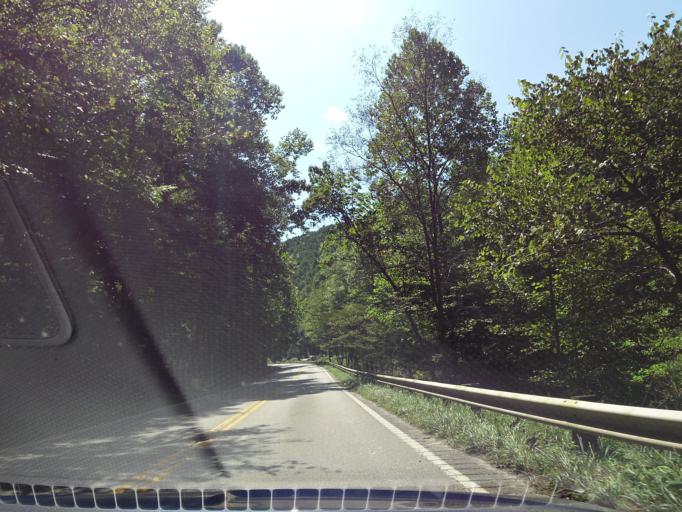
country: US
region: Kentucky
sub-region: Harlan County
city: Loyall
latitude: 36.9176
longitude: -83.3451
